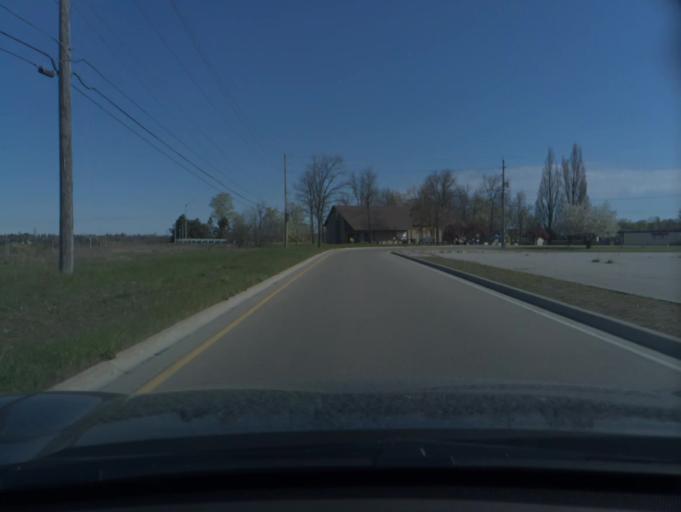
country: CA
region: Ontario
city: North Perth
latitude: 43.8365
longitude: -80.9999
